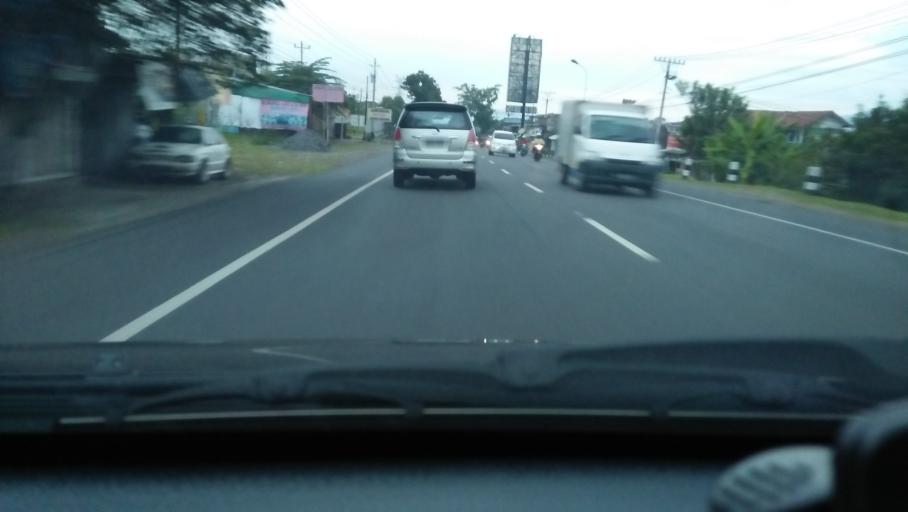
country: ID
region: Central Java
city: Magelang
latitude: -7.4133
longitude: 110.2359
